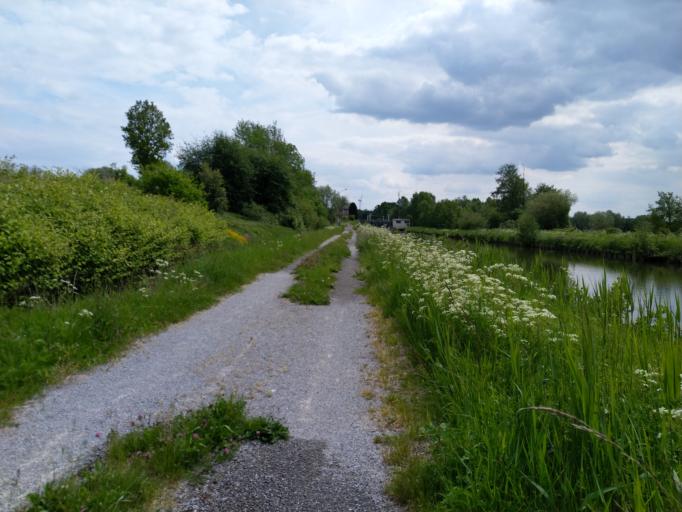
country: FR
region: Picardie
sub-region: Departement de l'Aisne
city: Wassigny
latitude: 50.0497
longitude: 3.6433
